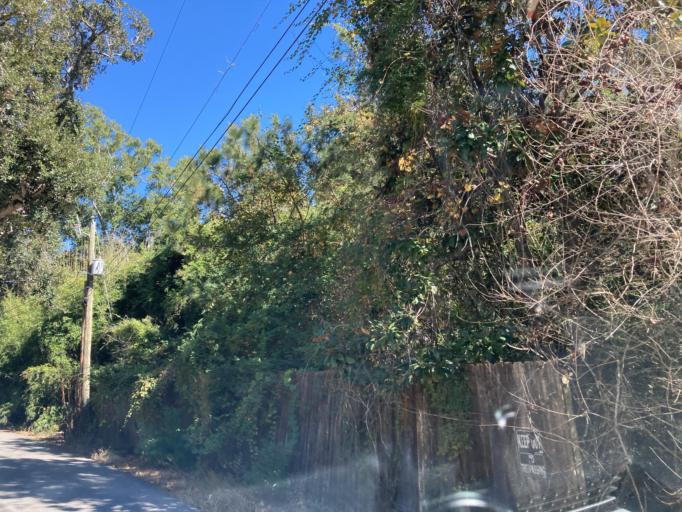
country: US
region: Mississippi
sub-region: Jackson County
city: Ocean Springs
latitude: 30.4098
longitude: -88.8174
